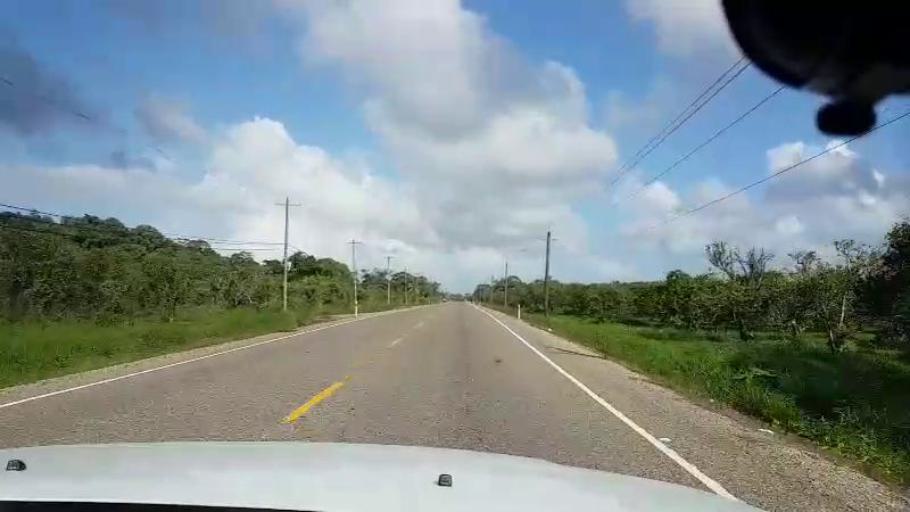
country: BZ
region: Stann Creek
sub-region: Dangriga
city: Dangriga
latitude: 16.9951
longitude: -88.3591
